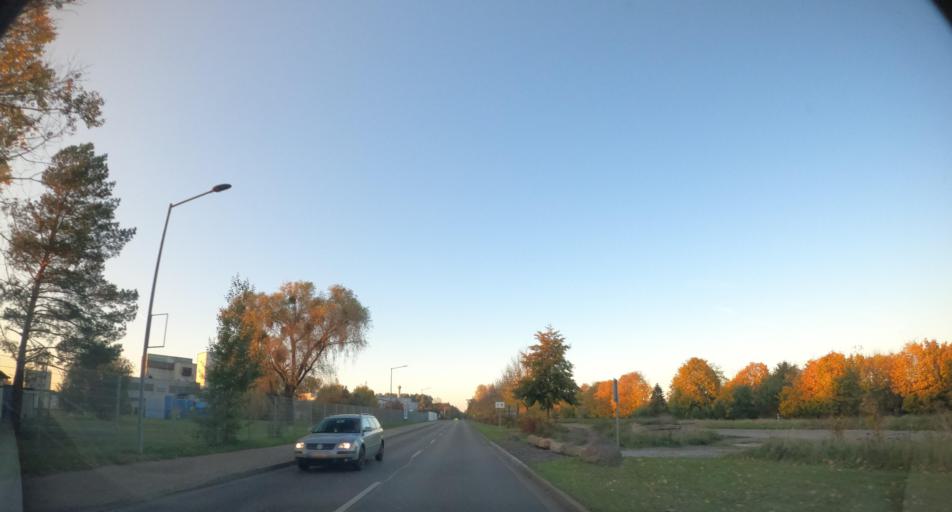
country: DE
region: Mecklenburg-Vorpommern
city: Ueckermunde
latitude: 53.7271
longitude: 14.0598
